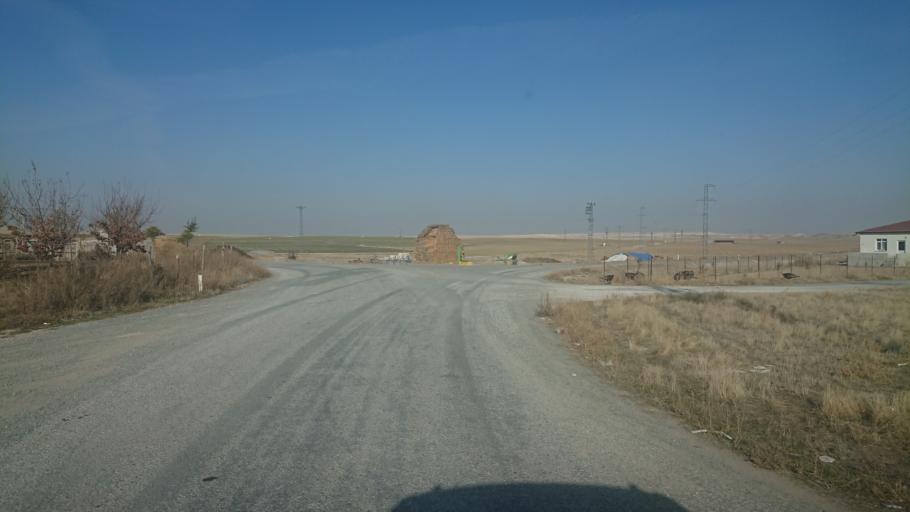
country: TR
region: Aksaray
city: Sultanhani
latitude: 38.0381
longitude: 33.6064
